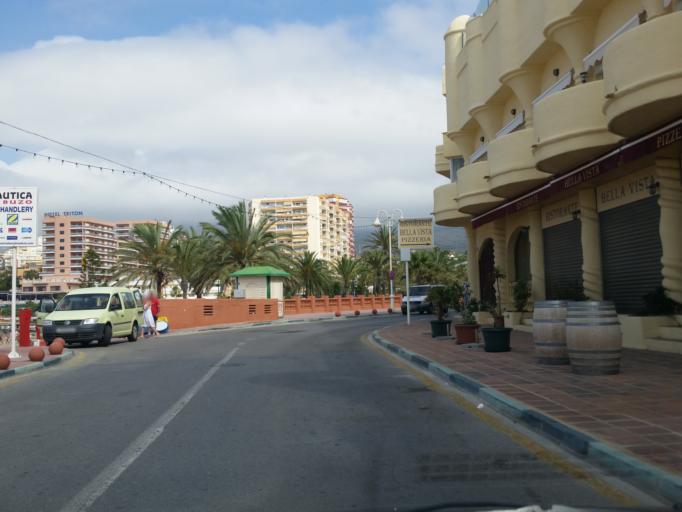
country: ES
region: Andalusia
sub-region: Provincia de Malaga
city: Torremolinos
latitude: 36.5954
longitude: -4.5146
